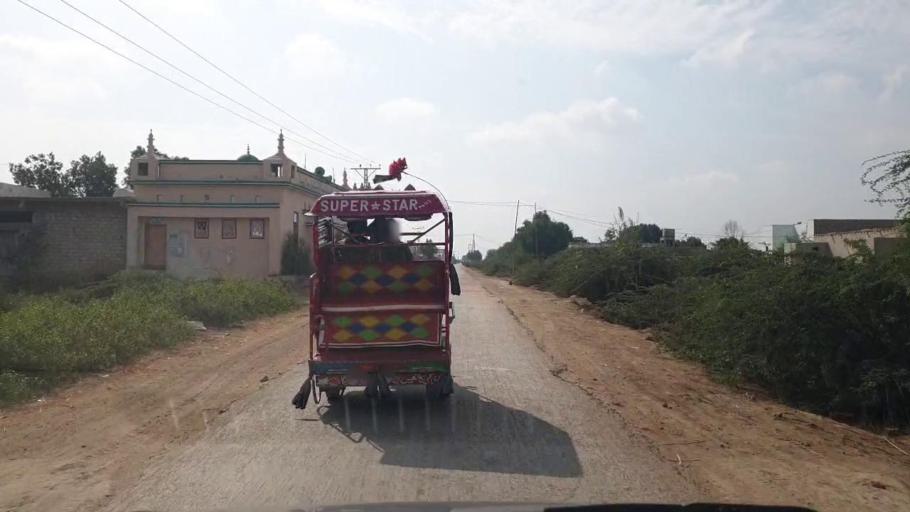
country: PK
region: Sindh
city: Kario
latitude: 24.6524
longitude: 68.5423
